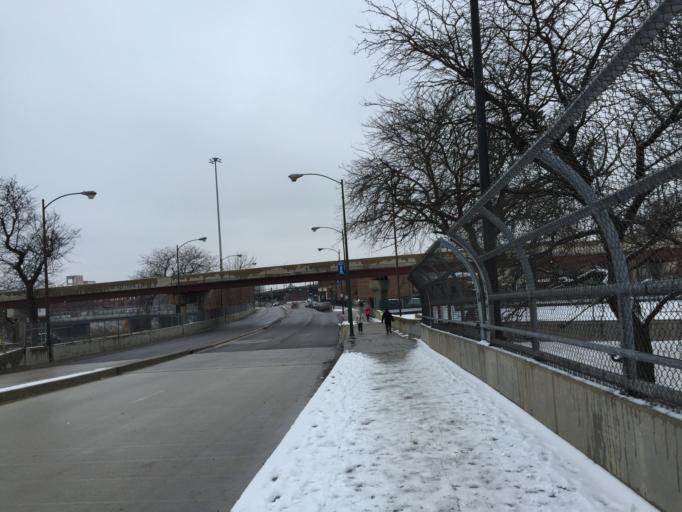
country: US
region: Illinois
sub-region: Cook County
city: Chicago
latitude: 41.8473
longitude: -87.6323
